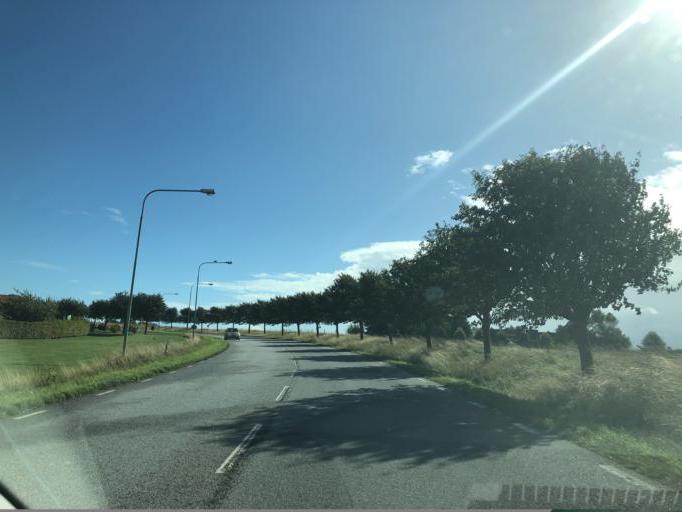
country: SE
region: Skane
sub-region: Helsingborg
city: Glumslov
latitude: 55.9376
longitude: 12.8056
